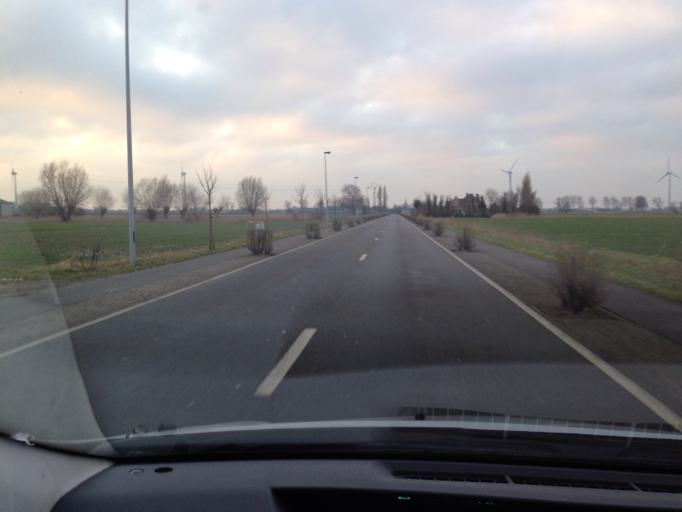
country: BE
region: Flanders
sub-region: Provincie West-Vlaanderen
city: Gistel
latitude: 51.1789
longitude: 2.9625
